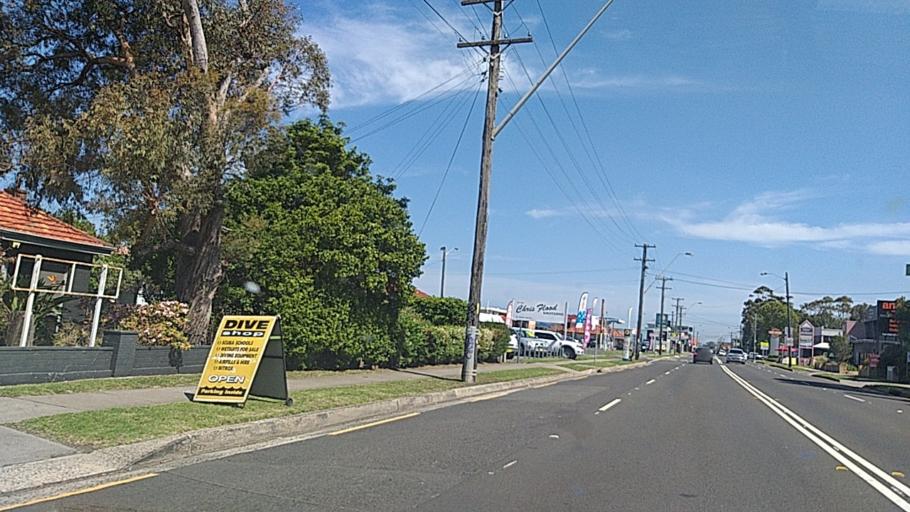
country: AU
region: New South Wales
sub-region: Wollongong
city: Fairy Meadow
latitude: -34.3882
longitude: 150.8941
